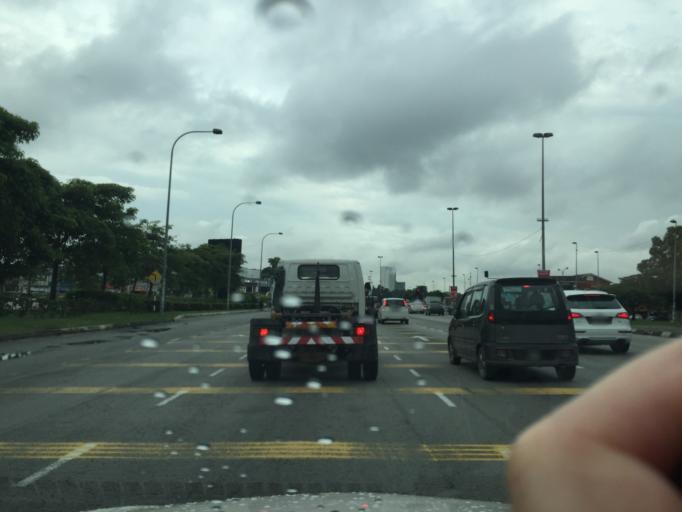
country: MY
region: Selangor
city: Klang
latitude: 2.9966
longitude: 101.4448
